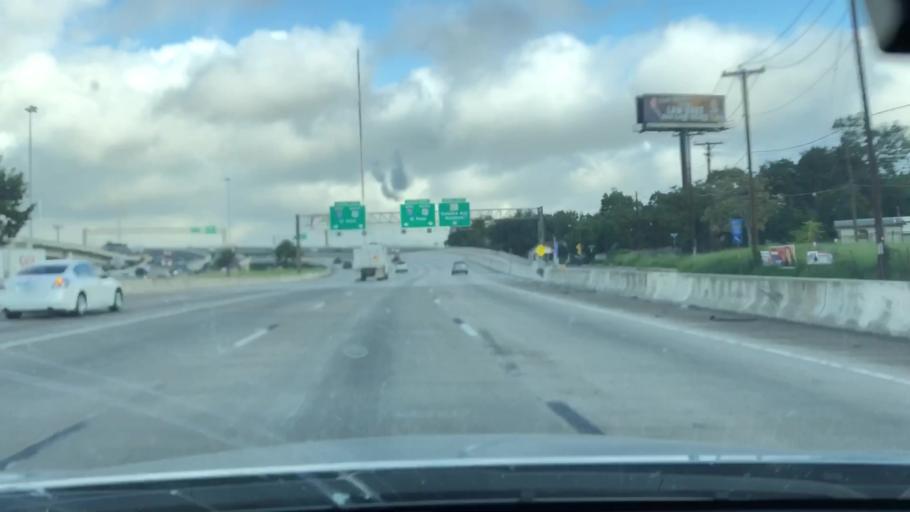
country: US
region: Texas
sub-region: Bexar County
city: San Antonio
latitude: 29.4365
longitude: -98.5038
